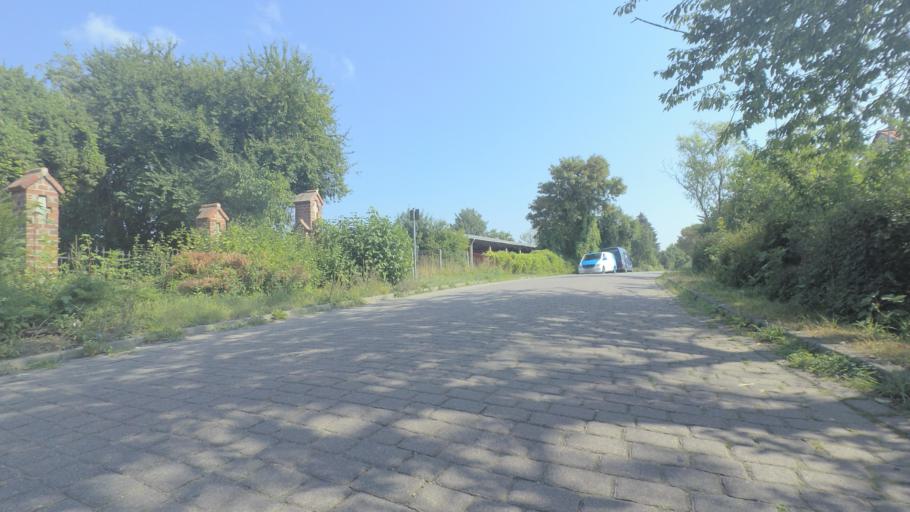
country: DE
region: Mecklenburg-Vorpommern
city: Pampow
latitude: 53.6833
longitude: 12.5666
